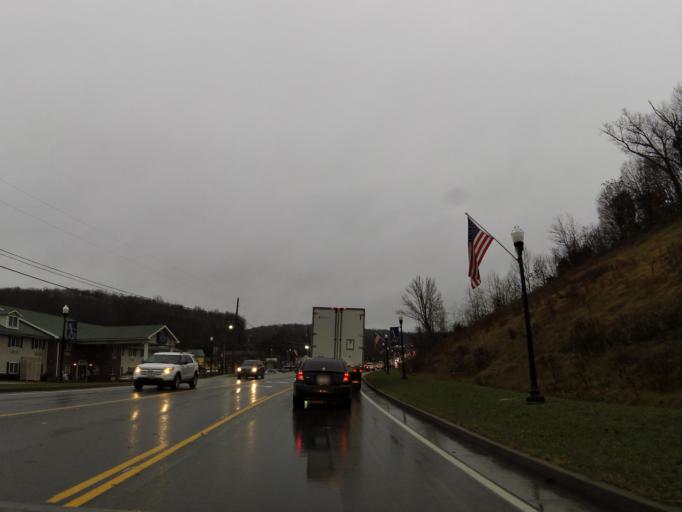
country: US
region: Kentucky
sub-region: Rockcastle County
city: Mount Vernon
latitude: 37.3833
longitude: -84.3304
